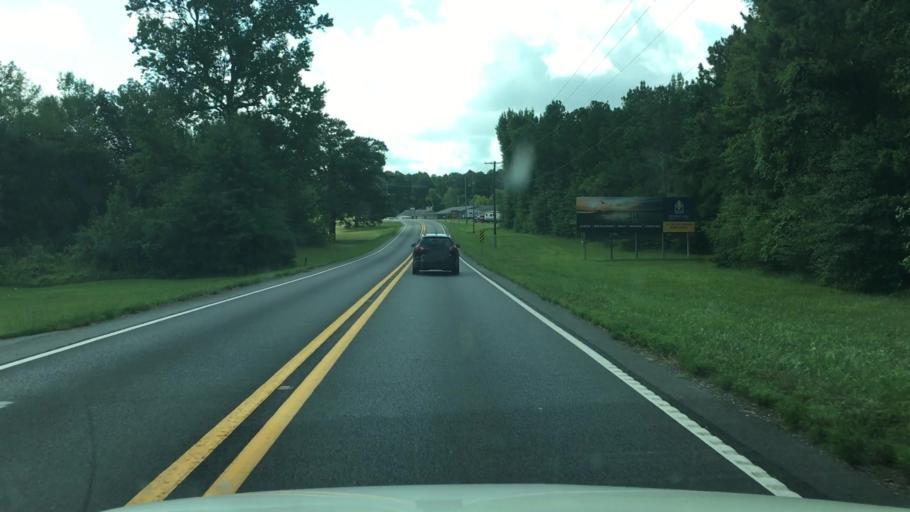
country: US
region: Arkansas
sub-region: Garland County
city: Lake Hamilton
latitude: 34.2701
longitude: -93.1457
